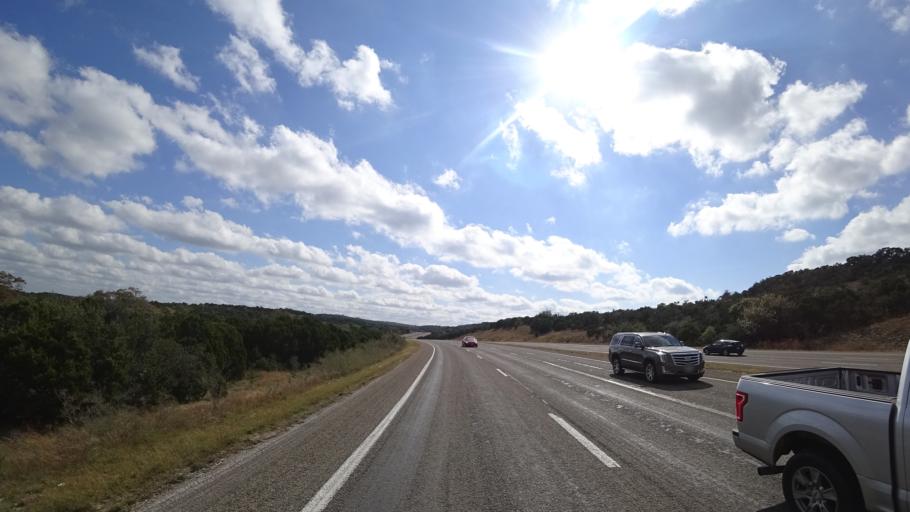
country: US
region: Texas
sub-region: Travis County
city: Barton Creek
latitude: 30.2713
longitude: -97.8964
